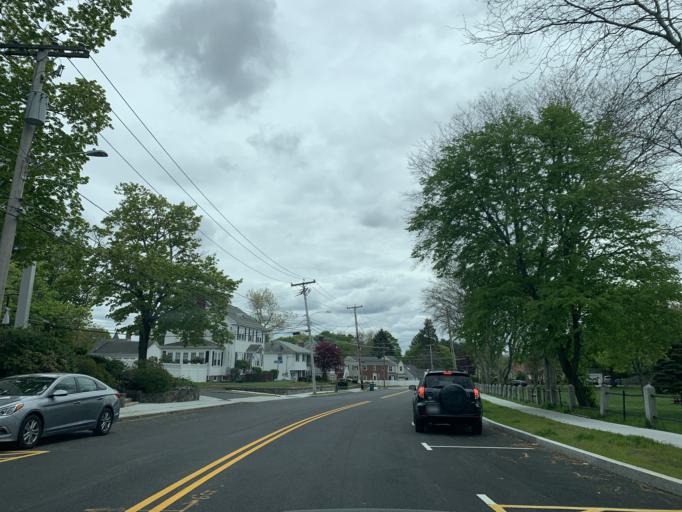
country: US
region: Massachusetts
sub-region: Norfolk County
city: Norwood
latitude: 42.1841
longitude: -71.2114
